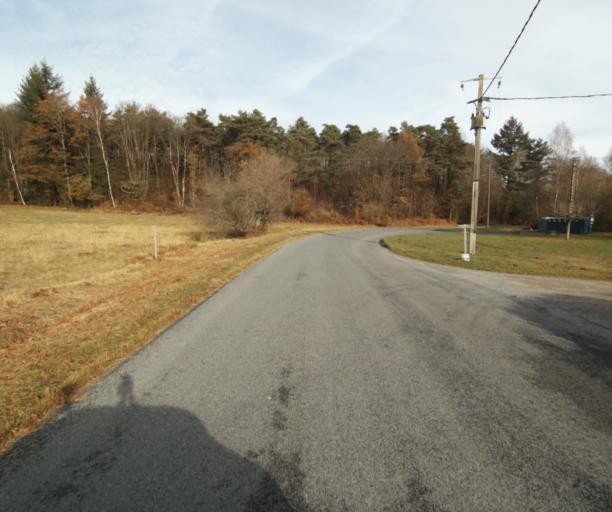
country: FR
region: Limousin
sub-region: Departement de la Correze
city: Sainte-Fortunade
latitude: 45.1781
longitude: 1.7452
